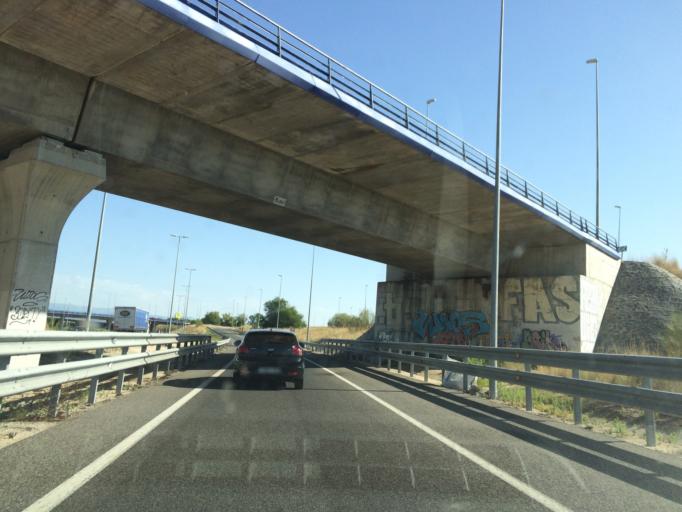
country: ES
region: Madrid
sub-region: Provincia de Madrid
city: Majadahonda
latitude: 40.4507
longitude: -3.8787
